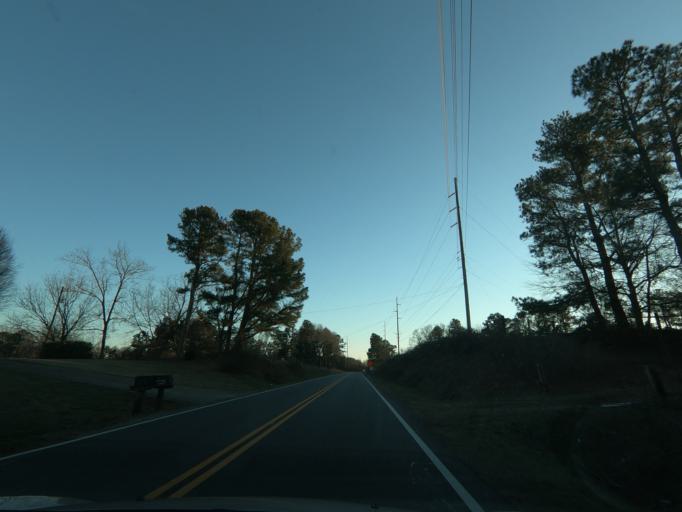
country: US
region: Georgia
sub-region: Forsyth County
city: Cumming
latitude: 34.3061
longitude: -84.1502
